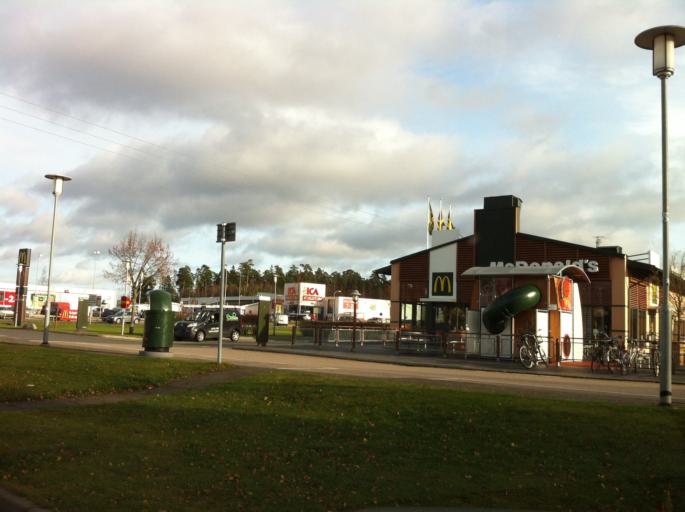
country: SE
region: Kronoberg
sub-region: Vaxjo Kommun
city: Vaexjoe
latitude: 56.8606
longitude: 14.7319
